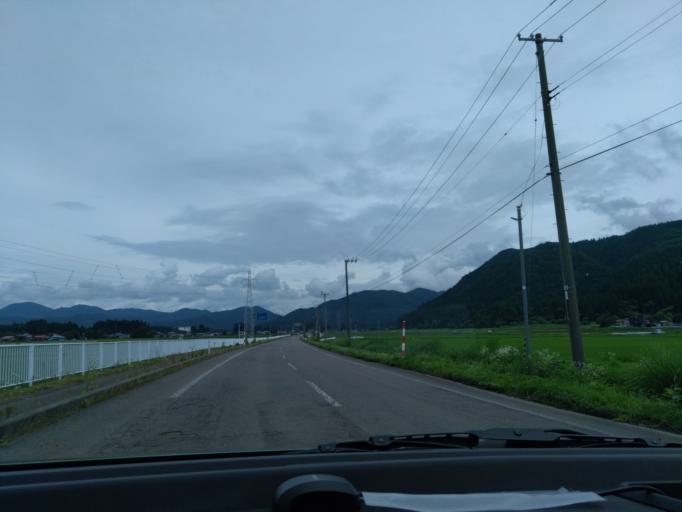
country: JP
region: Akita
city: Kakunodatemachi
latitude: 39.5943
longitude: 140.6150
